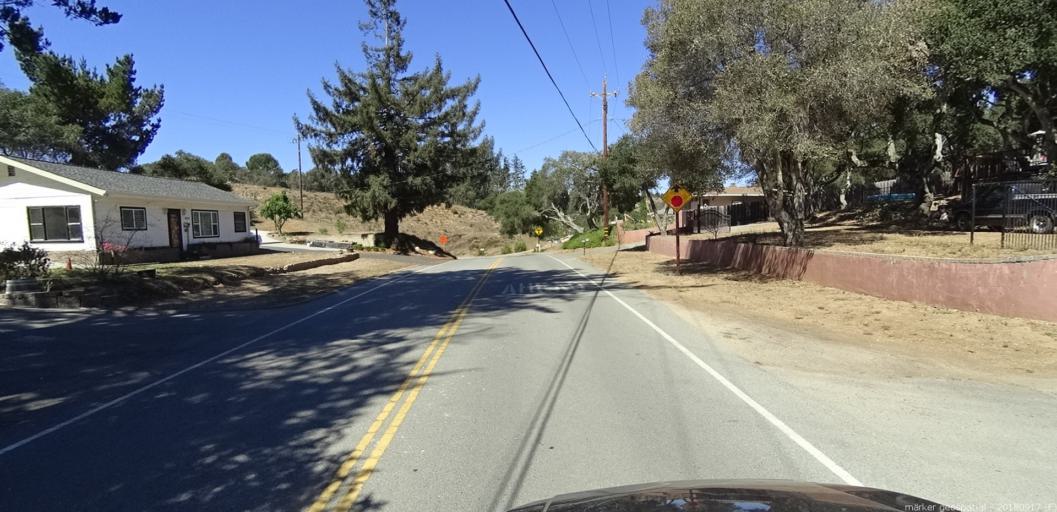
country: US
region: California
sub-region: Monterey County
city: Prunedale
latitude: 36.8234
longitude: -121.6330
